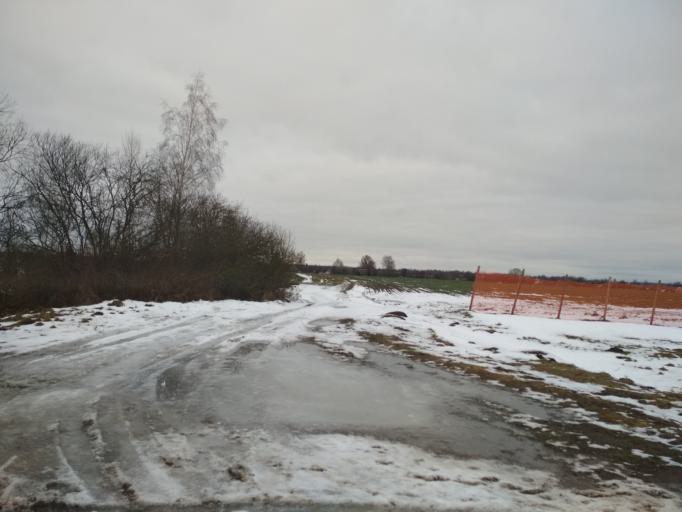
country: BY
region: Minsk
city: Mar''ina Horka
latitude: 53.5025
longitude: 28.0774
